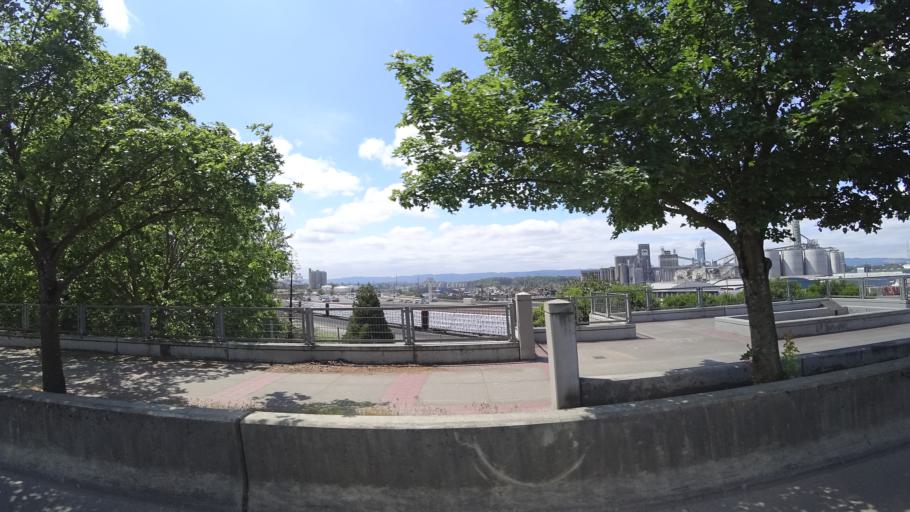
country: US
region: Washington
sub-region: Clark County
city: Vancouver
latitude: 45.6330
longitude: -122.6853
